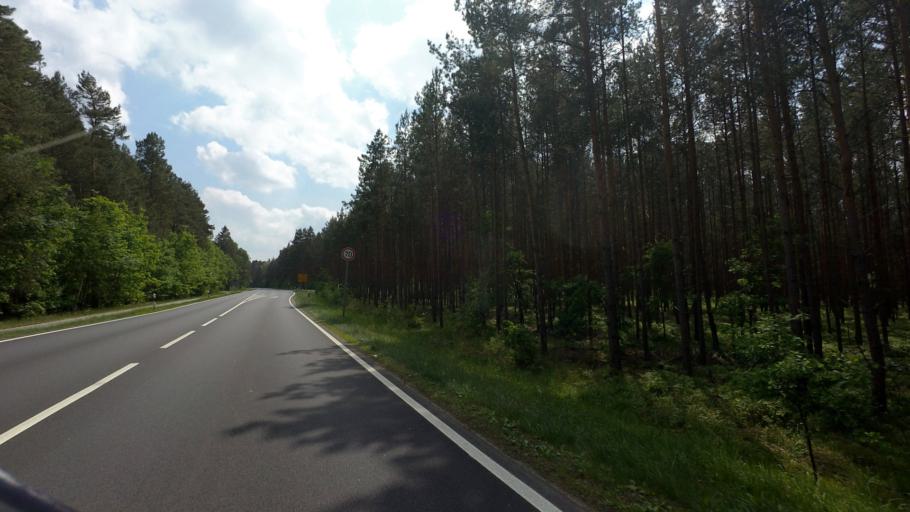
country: DE
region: Saxony
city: Rietschen
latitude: 51.3484
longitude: 14.8038
